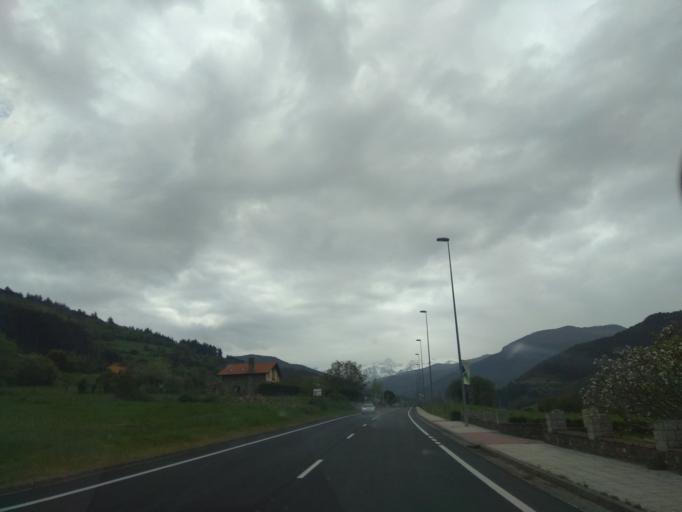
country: ES
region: Cantabria
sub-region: Provincia de Cantabria
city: Potes
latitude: 43.1701
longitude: -4.6031
